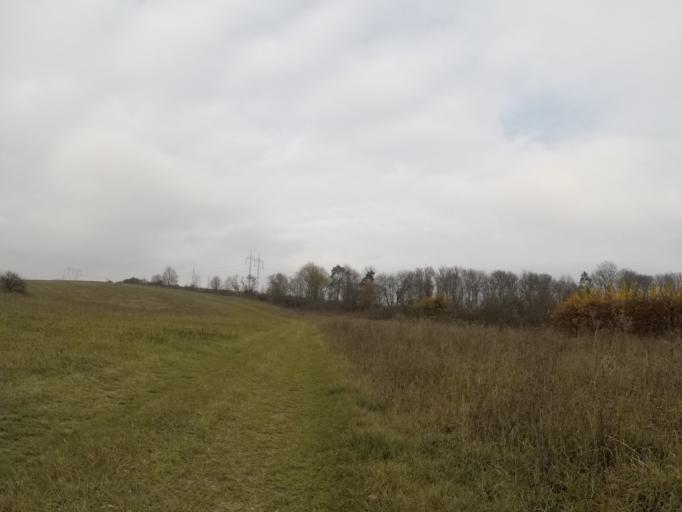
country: SK
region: Presovsky
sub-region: Okres Presov
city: Presov
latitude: 48.9020
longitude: 21.1846
